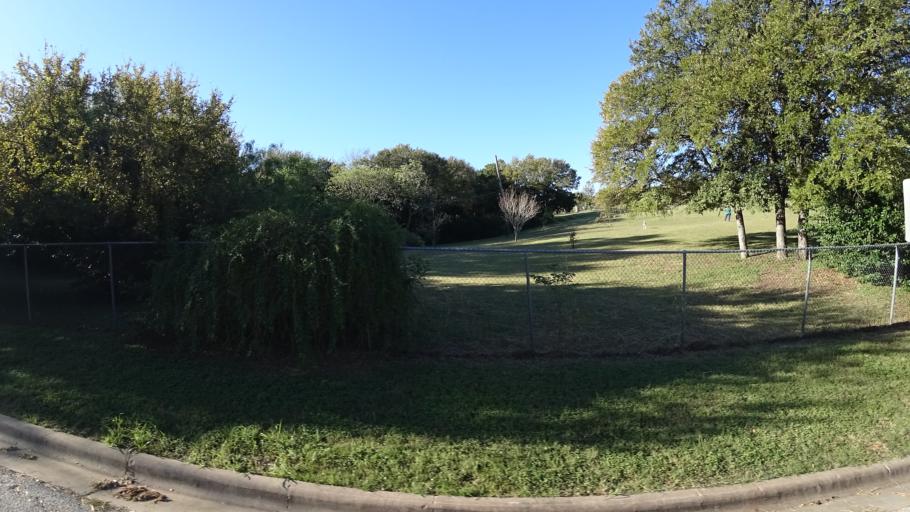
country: US
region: Texas
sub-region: Travis County
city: Austin
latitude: 30.3058
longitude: -97.6742
